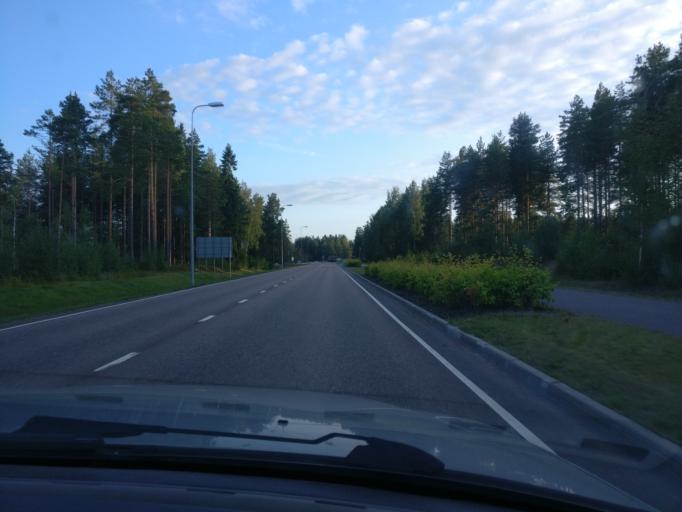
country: FI
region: Kymenlaakso
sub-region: Kotka-Hamina
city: Broby
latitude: 60.5004
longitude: 26.7406
